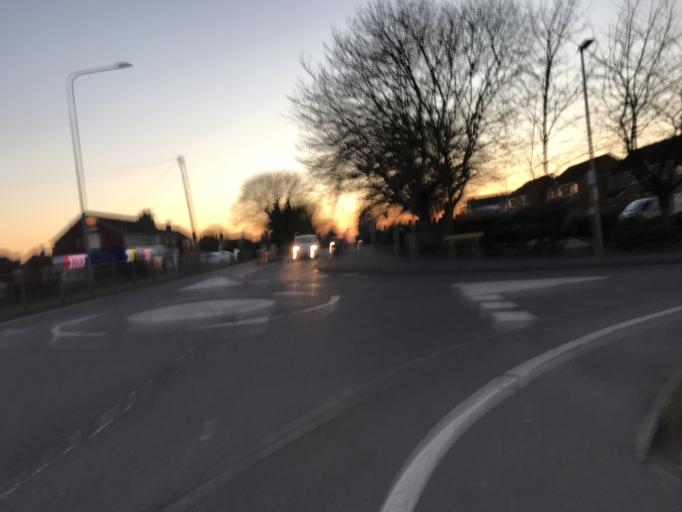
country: GB
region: England
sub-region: Lincolnshire
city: Holton le Clay
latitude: 53.5236
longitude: -0.0648
